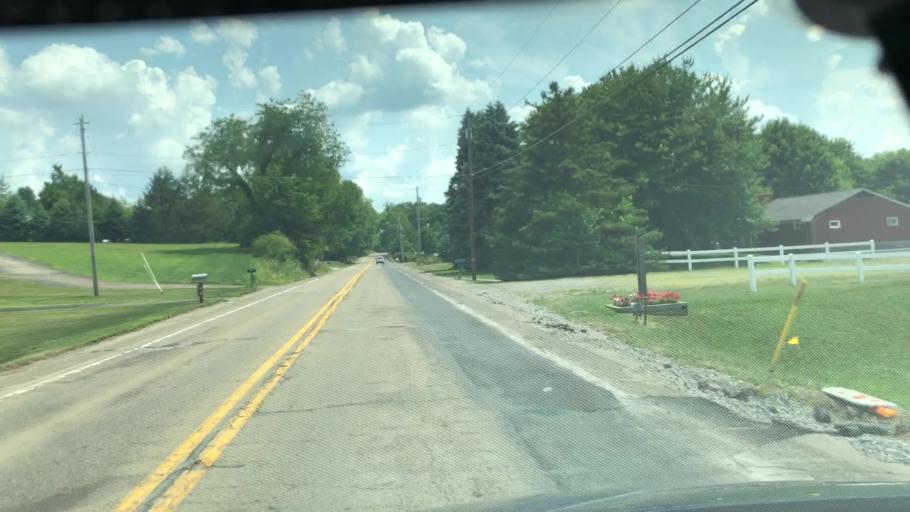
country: US
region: Pennsylvania
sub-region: Butler County
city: Saxonburg
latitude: 40.7672
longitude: -79.7858
